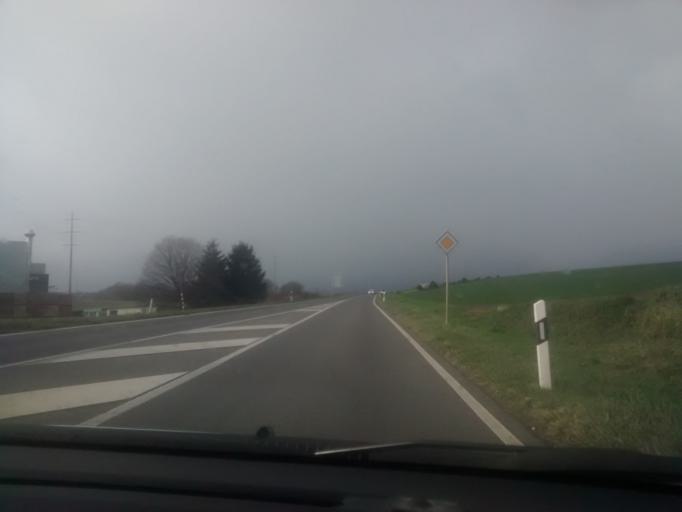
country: CH
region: Vaud
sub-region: Jura-Nord vaudois District
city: Montagny
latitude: 46.7890
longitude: 6.6027
